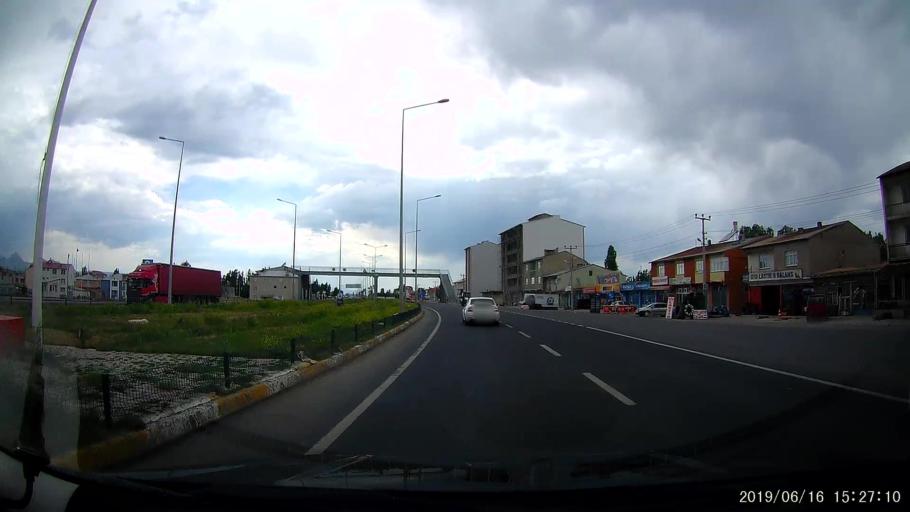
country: TR
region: Erzurum
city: Horasan
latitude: 40.0373
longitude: 42.1633
